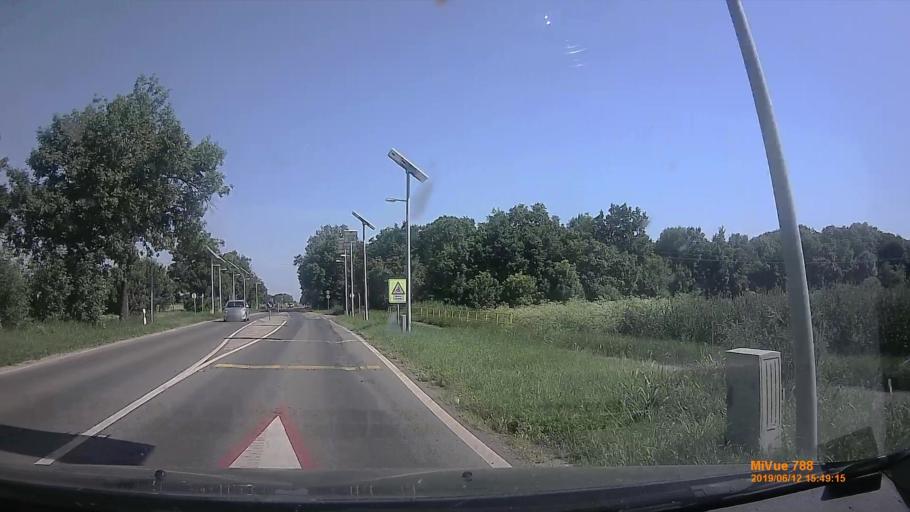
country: HU
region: Csongrad
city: Apatfalva
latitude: 46.1976
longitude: 20.5554
